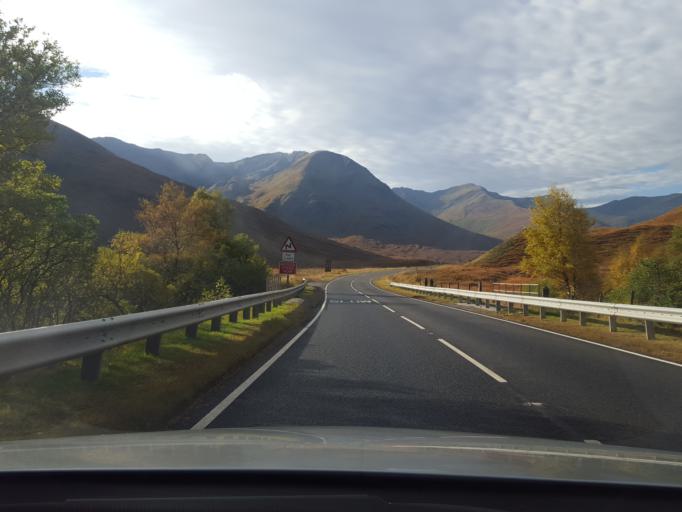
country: GB
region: Scotland
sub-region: Highland
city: Fort William
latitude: 57.1576
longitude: -5.1706
